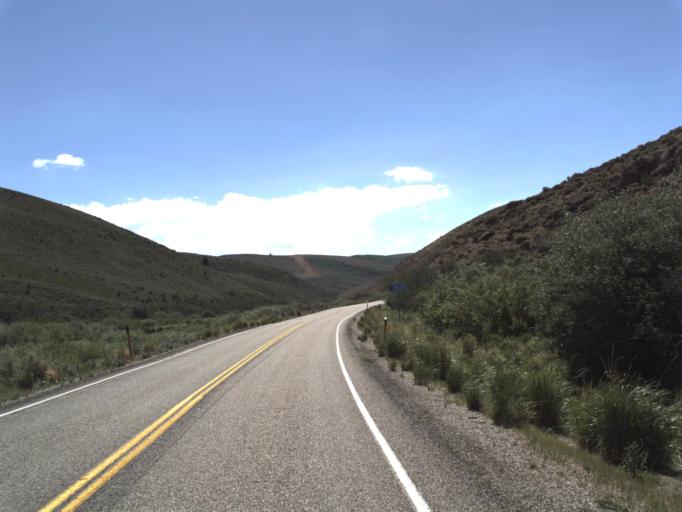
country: US
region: Utah
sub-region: Rich County
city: Randolph
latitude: 41.4926
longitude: -111.3319
